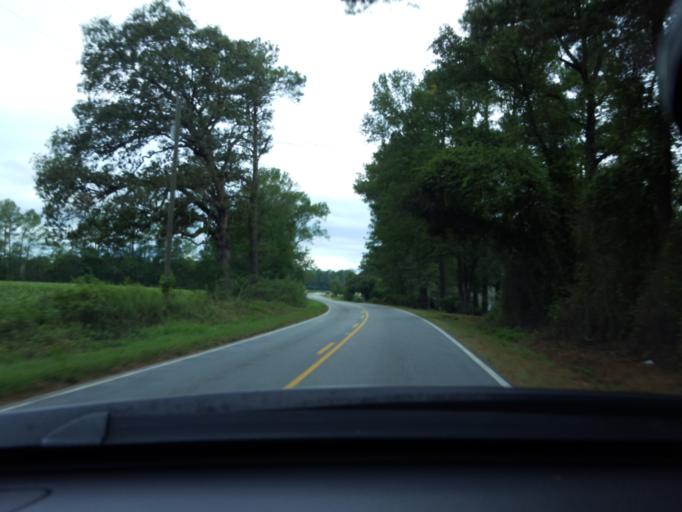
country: US
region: North Carolina
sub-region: Sampson County
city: Clinton
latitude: 34.7825
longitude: -78.3648
